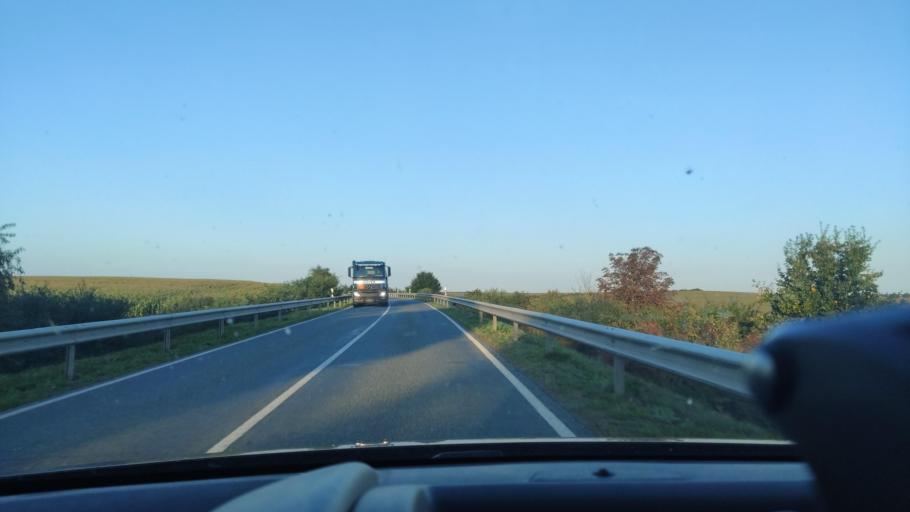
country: DE
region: Mecklenburg-Vorpommern
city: Lalendorf
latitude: 53.6172
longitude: 12.4088
